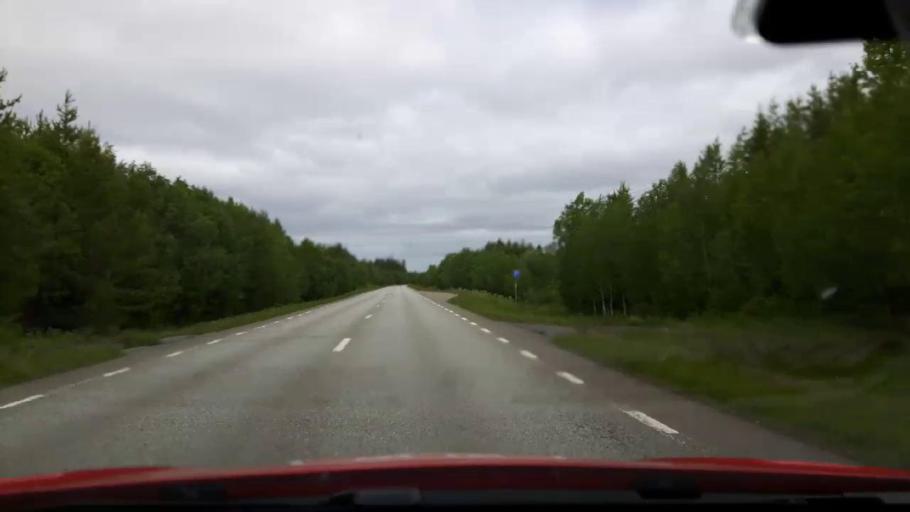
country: SE
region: Jaemtland
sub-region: Krokoms Kommun
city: Krokom
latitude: 63.5603
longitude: 14.6061
